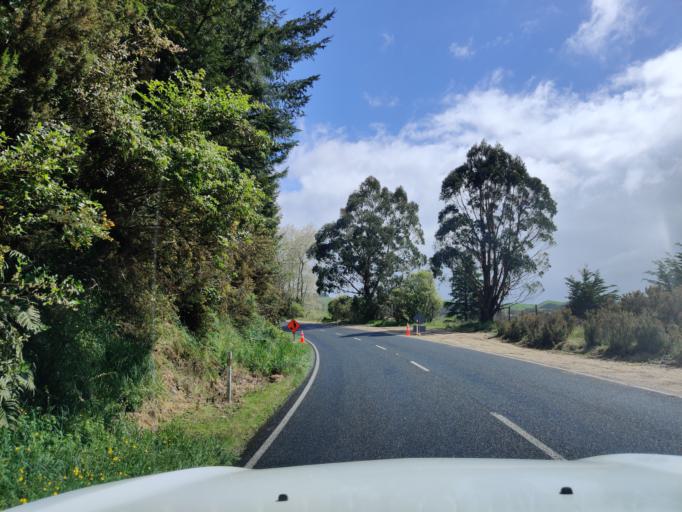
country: NZ
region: Bay of Plenty
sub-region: Rotorua District
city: Rotorua
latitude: -38.1760
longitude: 176.3259
